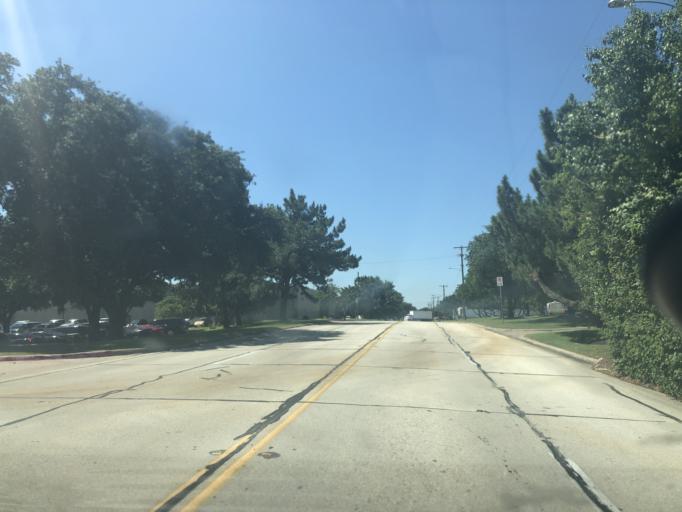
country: US
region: Texas
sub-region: Tarrant County
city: Euless
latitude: 32.7919
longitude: -97.0421
